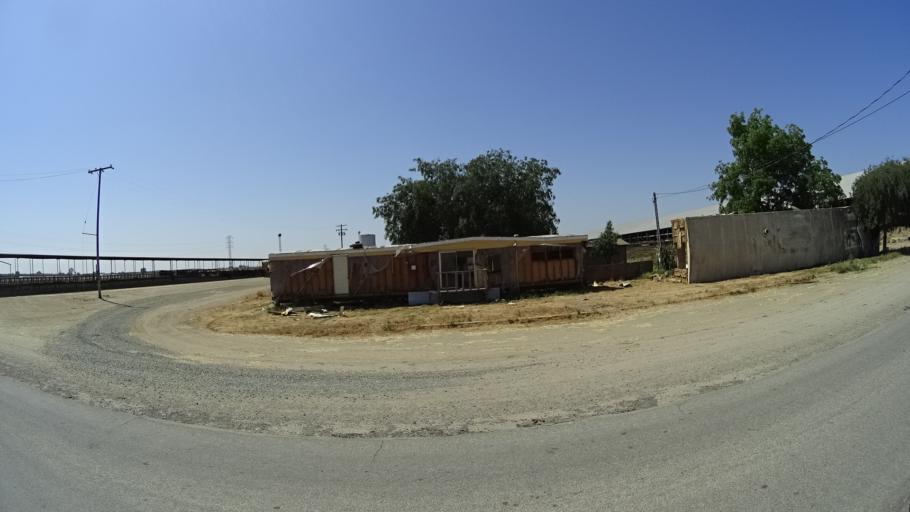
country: US
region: California
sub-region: Kings County
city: Hanford
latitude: 36.3717
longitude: -119.5934
